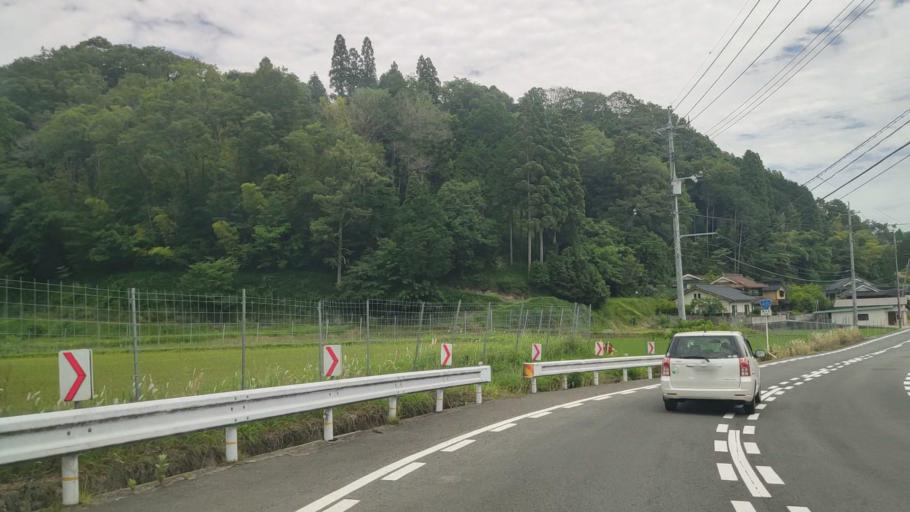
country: JP
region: Hyogo
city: Yamazakicho-nakabirose
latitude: 35.1021
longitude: 134.3125
